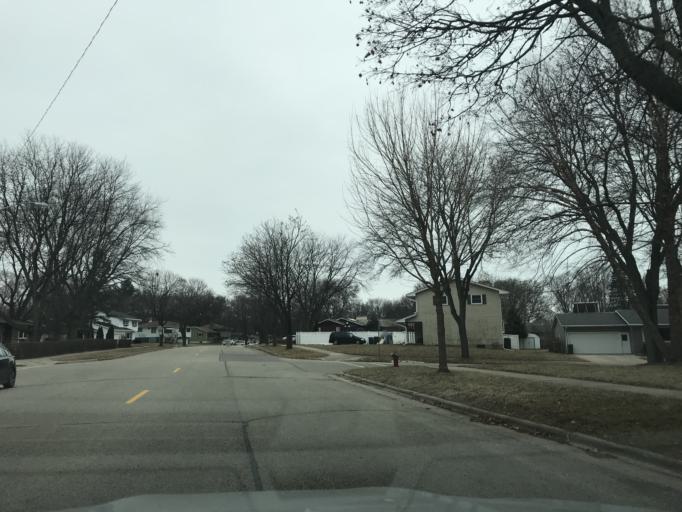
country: US
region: Wisconsin
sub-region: Dane County
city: Monona
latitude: 43.0933
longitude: -89.2981
